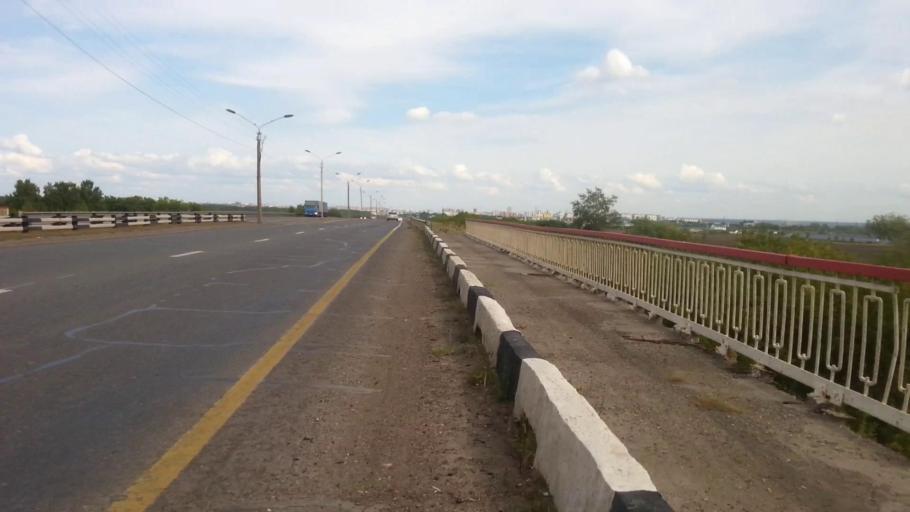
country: RU
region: Altai Krai
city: Vlasikha
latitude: 53.3514
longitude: 83.5863
